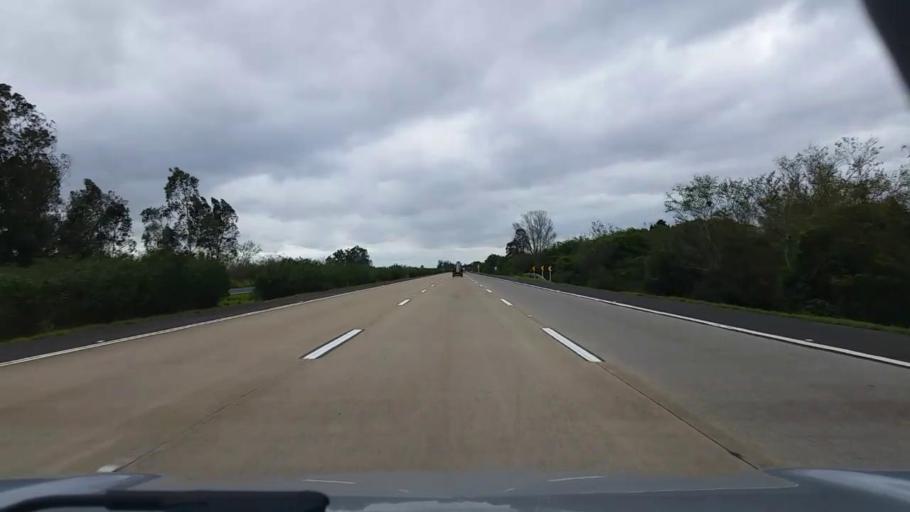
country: BR
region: Rio Grande do Sul
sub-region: Rolante
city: Rolante
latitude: -29.8854
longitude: -50.5814
